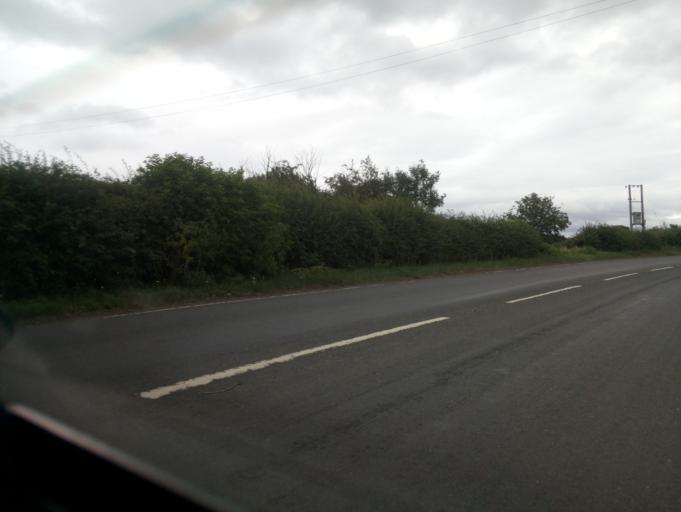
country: GB
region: England
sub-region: Worcestershire
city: Kempsey
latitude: 52.1593
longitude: -2.2145
